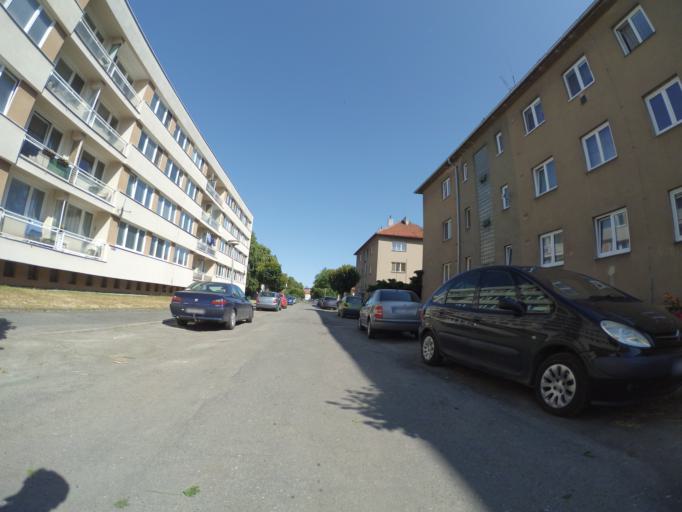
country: CZ
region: Central Bohemia
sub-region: Okres Nymburk
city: Podebrady
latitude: 50.1512
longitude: 15.1149
